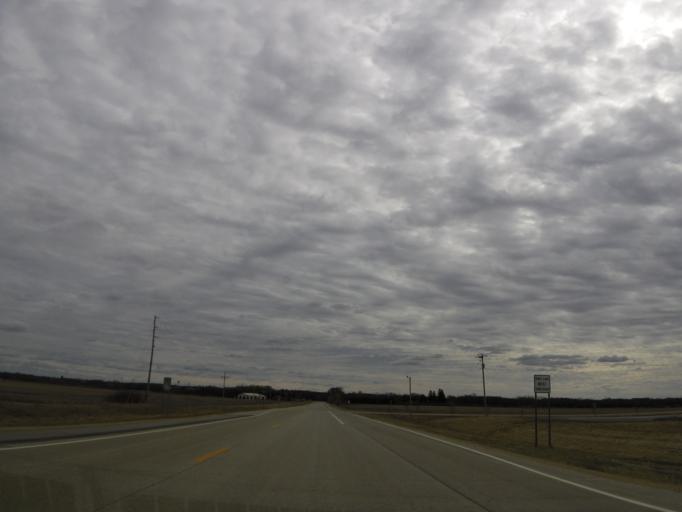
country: US
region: Minnesota
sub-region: Fillmore County
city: Spring Valley
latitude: 43.5089
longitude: -92.3694
